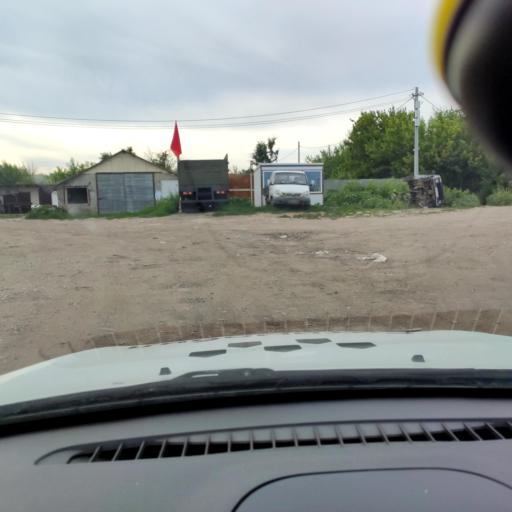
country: RU
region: Samara
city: Tol'yatti
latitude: 53.5370
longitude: 49.4383
